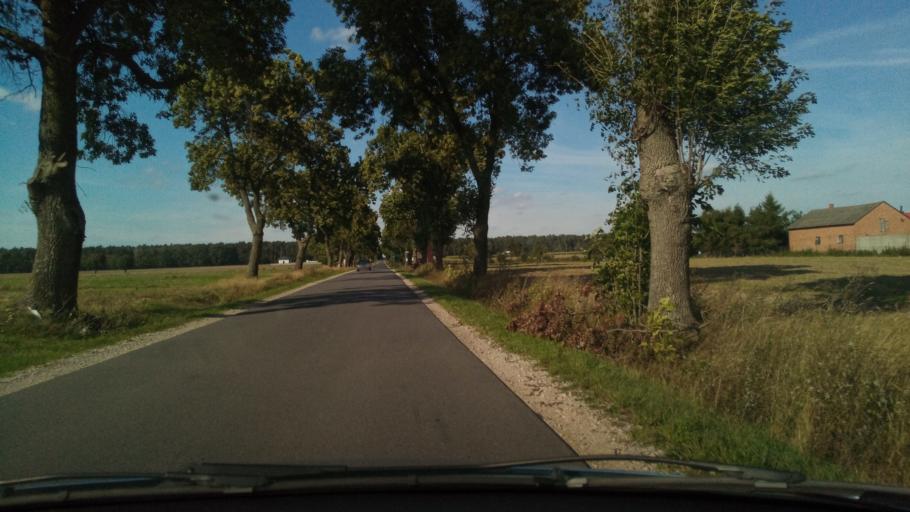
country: PL
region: Lodz Voivodeship
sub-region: Powiat piotrkowski
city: Sulejow
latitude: 51.4006
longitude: 19.8235
